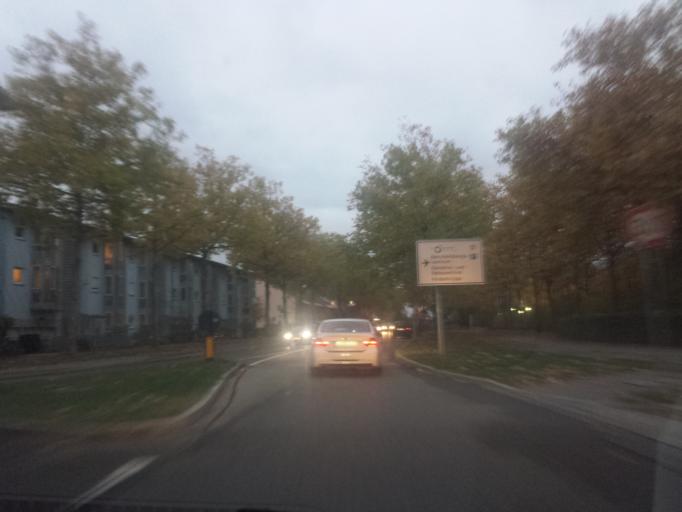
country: DE
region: Bavaria
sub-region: Upper Bavaria
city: Gaimersheim
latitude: 48.7698
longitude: 11.3804
